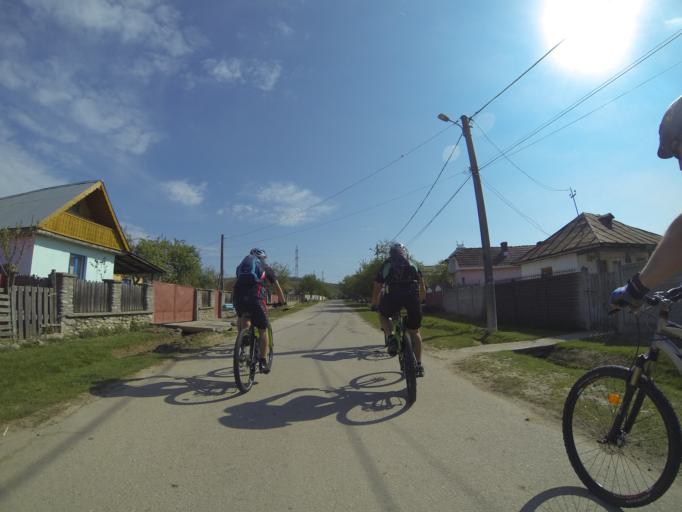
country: RO
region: Dolj
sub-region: Comuna Bradesti
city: Bradesti
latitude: 44.5165
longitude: 23.6055
